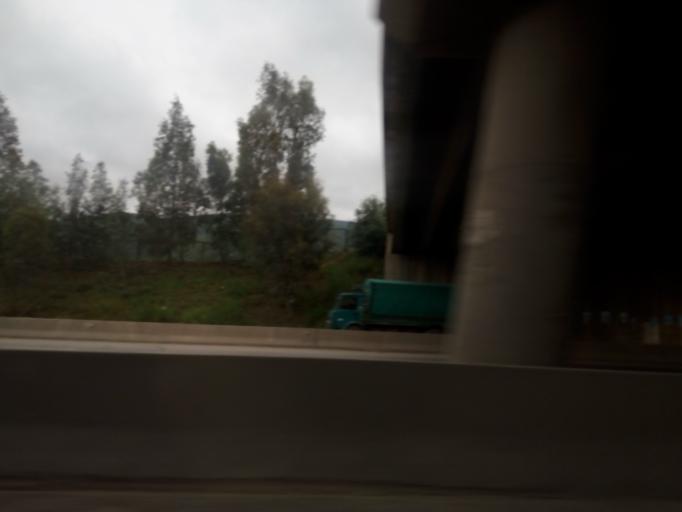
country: DZ
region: Bouira
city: Lakhdaria
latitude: 36.5523
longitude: 3.6039
